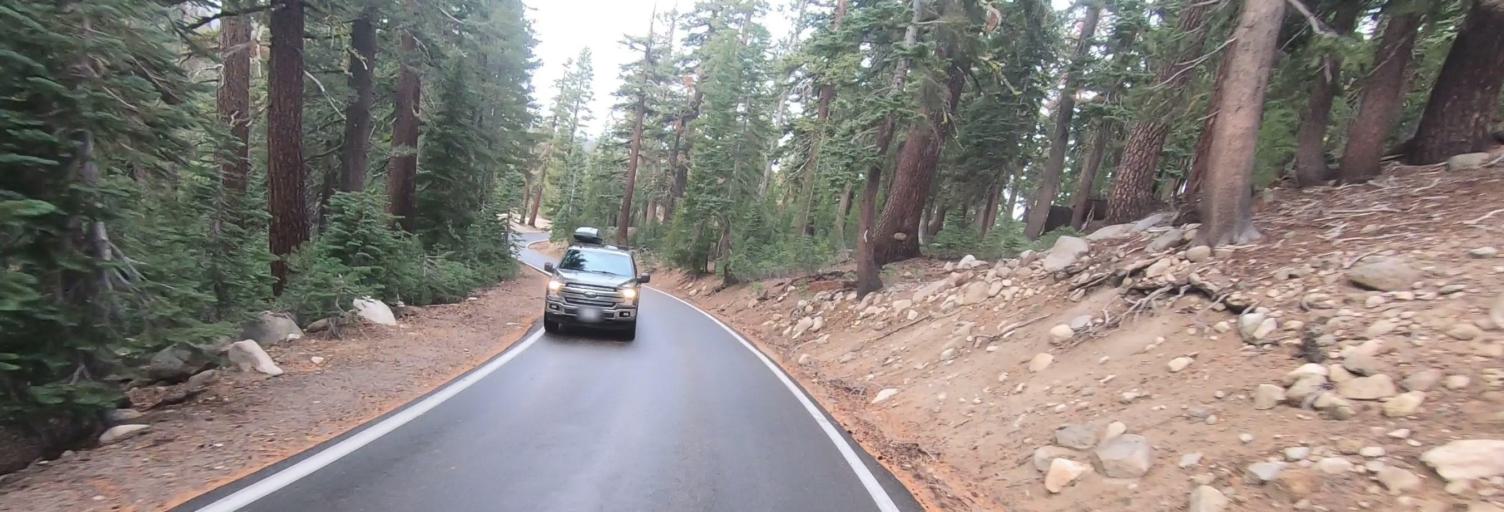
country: US
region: Nevada
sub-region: Douglas County
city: Gardnerville Ranchos
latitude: 38.5543
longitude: -119.8045
